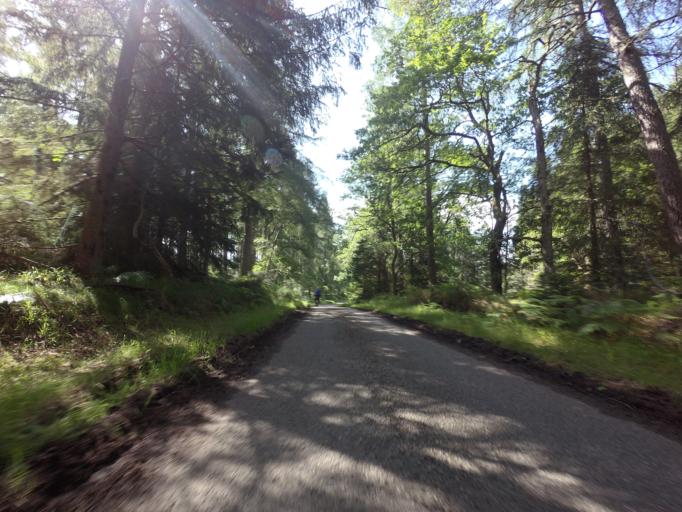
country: GB
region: Scotland
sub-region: Highland
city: Nairn
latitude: 57.5048
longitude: -3.9095
